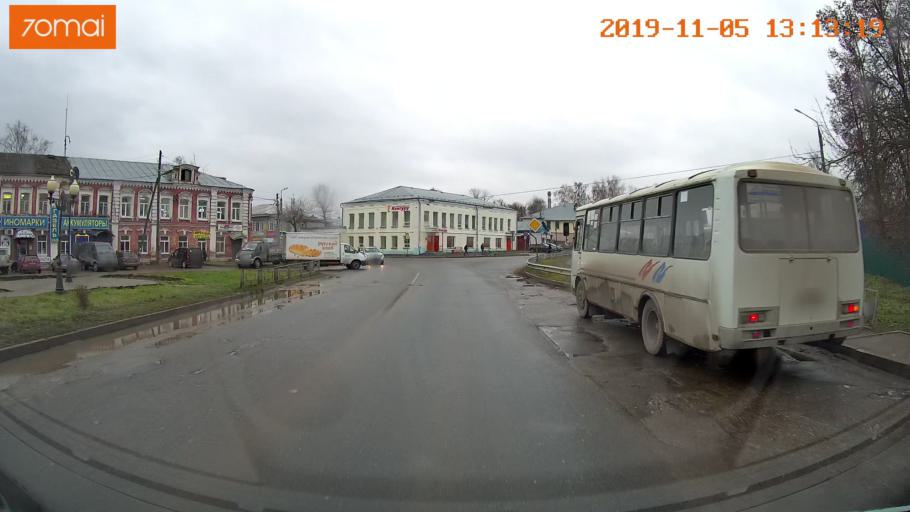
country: RU
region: Ivanovo
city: Shuya
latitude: 56.8517
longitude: 41.3538
